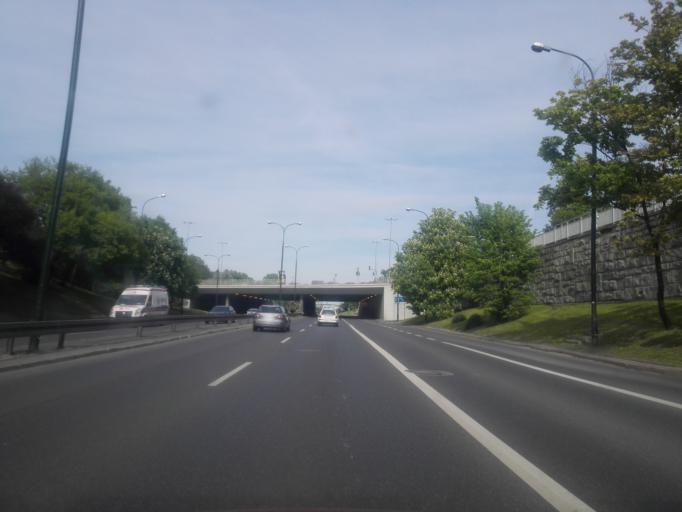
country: PL
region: Masovian Voivodeship
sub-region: Warszawa
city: Srodmiescie
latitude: 52.2187
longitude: 21.0233
